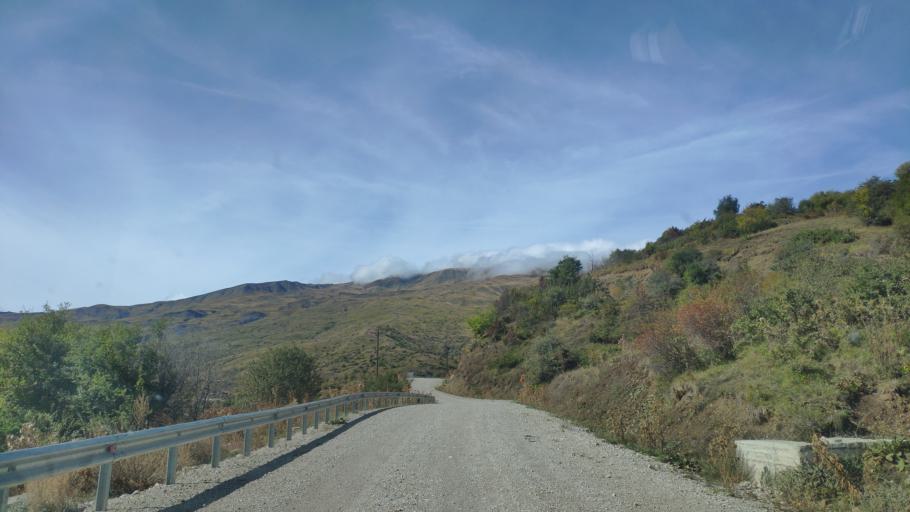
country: AL
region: Korce
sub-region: Rrethi i Devollit
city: Miras
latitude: 40.3981
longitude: 20.8425
